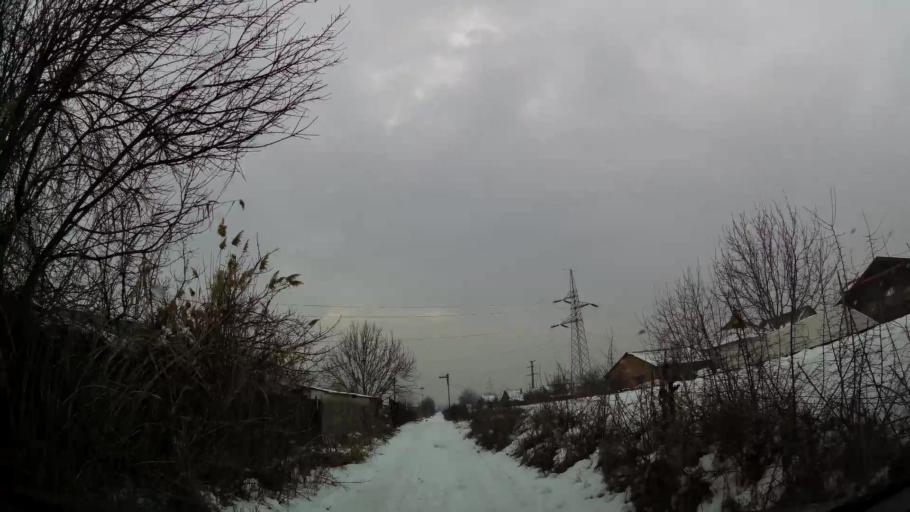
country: MK
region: Saraj
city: Saraj
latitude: 42.0426
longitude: 21.3529
